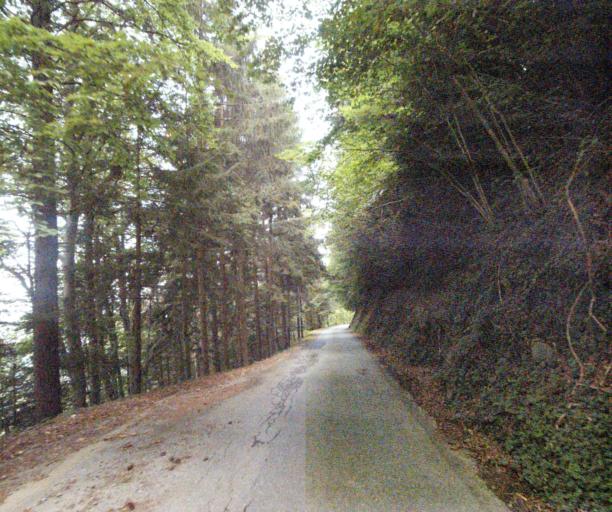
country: CH
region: Vaud
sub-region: Aigle District
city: Villeneuve
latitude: 46.4070
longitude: 6.9386
